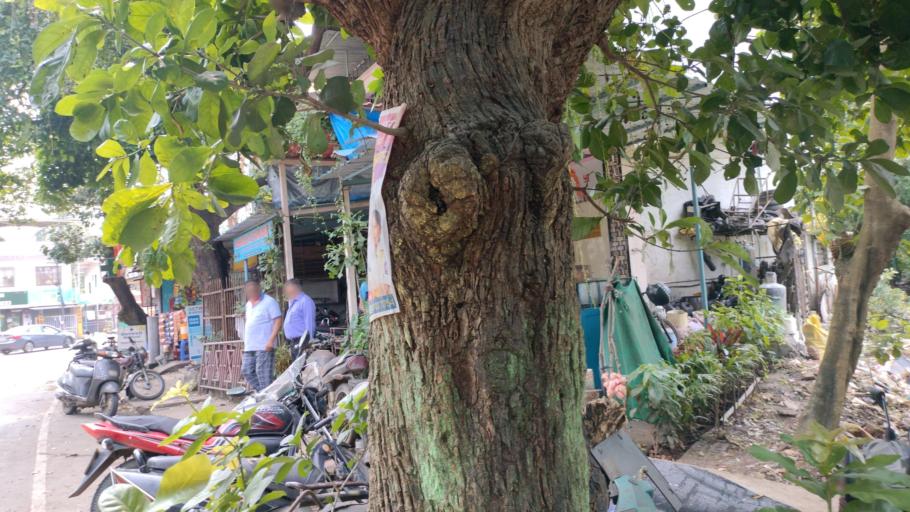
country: IN
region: Maharashtra
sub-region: Thane
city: Bhayandar
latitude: 19.3618
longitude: 72.8009
